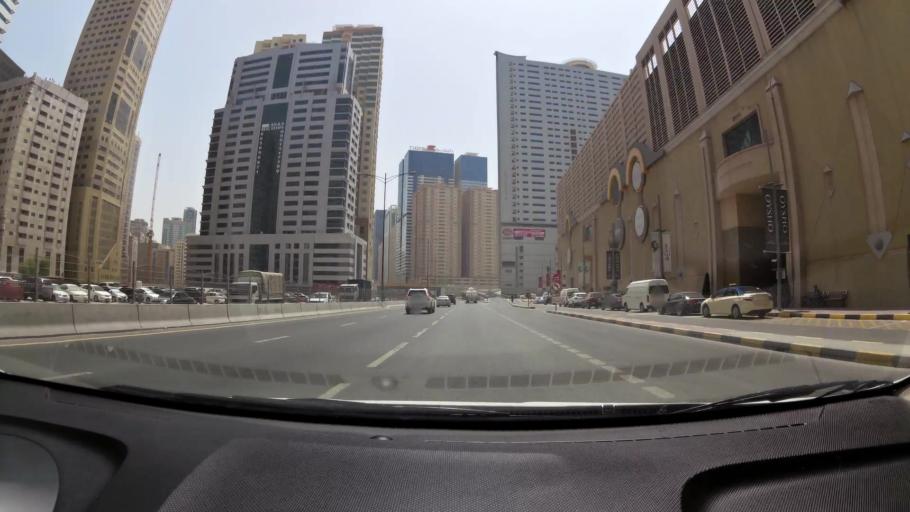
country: AE
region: Ash Shariqah
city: Sharjah
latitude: 25.2986
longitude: 55.3748
